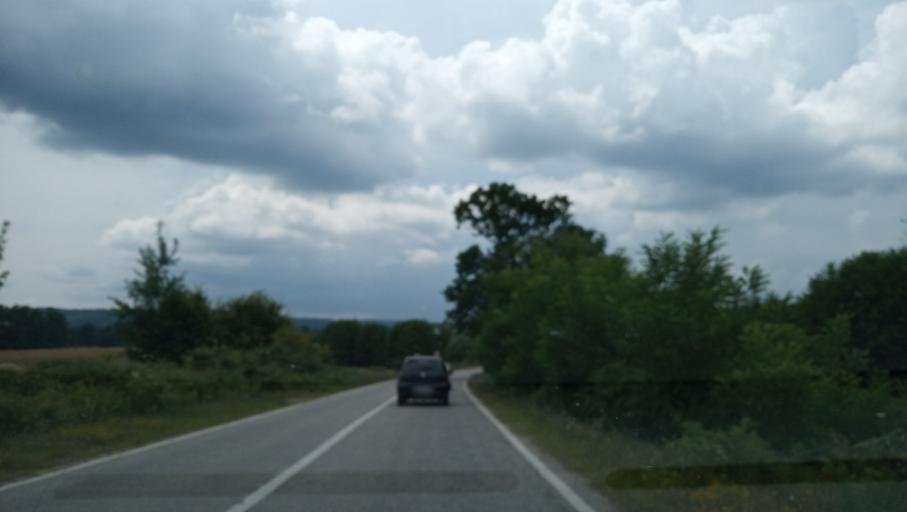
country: RO
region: Gorj
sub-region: Comuna Pestisani
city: Pestisani
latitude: 45.0592
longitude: 23.0129
